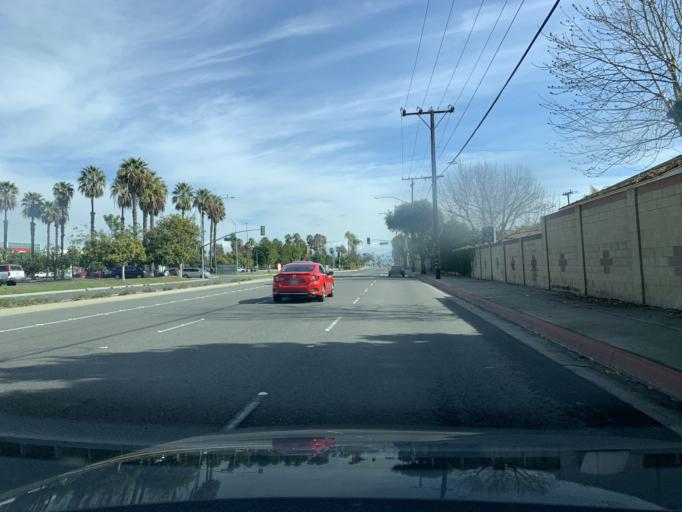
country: US
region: California
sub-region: Orange County
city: Westminster
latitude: 33.7443
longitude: -118.0144
